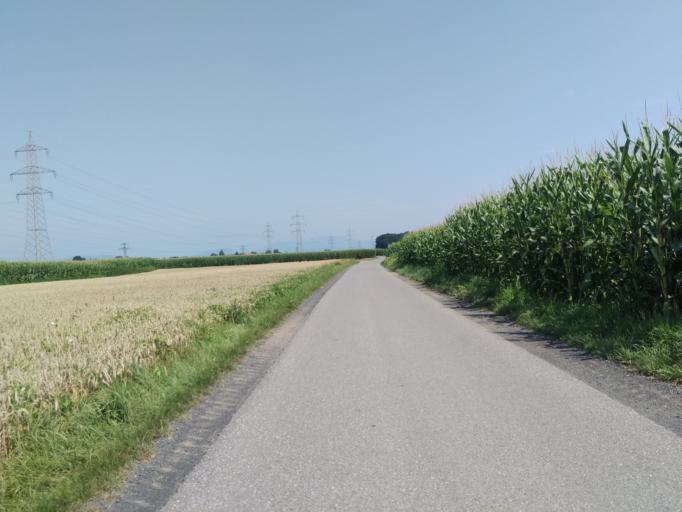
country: AT
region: Styria
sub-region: Politischer Bezirk Graz-Umgebung
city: Werndorf
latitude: 46.9291
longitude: 15.4899
